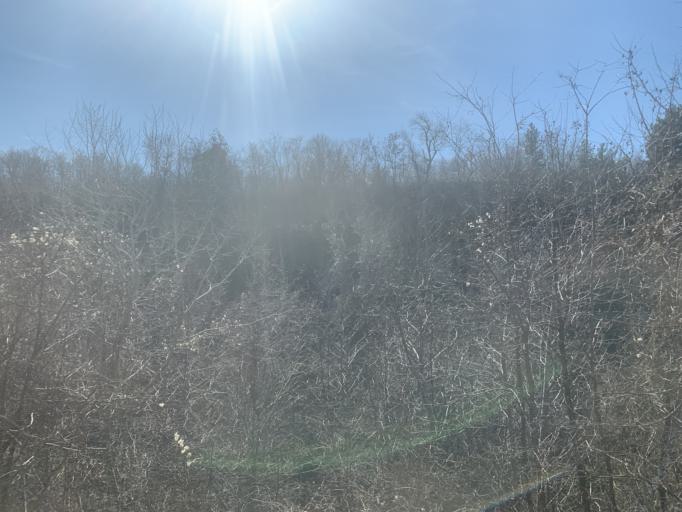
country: BG
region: Pazardzhik
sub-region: Obshtina Belovo
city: Belovo
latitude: 42.2103
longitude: 24.0305
